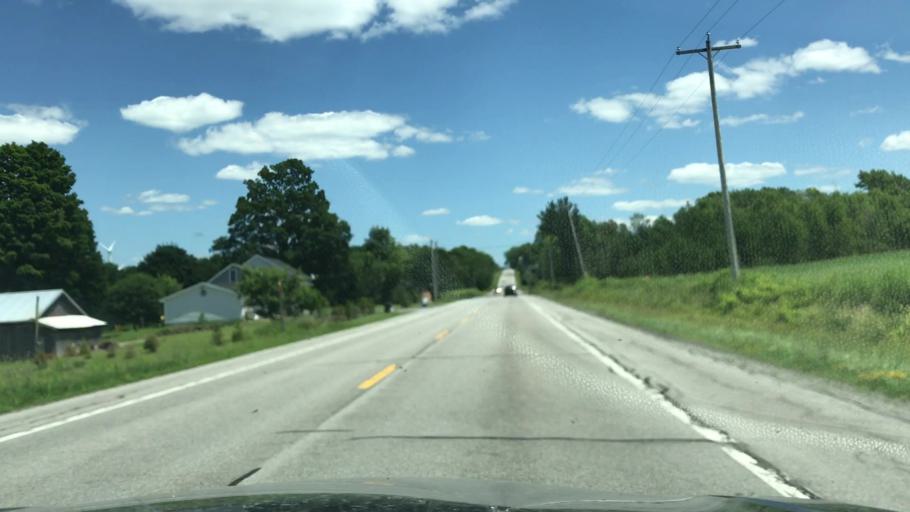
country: US
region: New York
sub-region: Wyoming County
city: Attica
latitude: 42.7536
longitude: -78.2658
